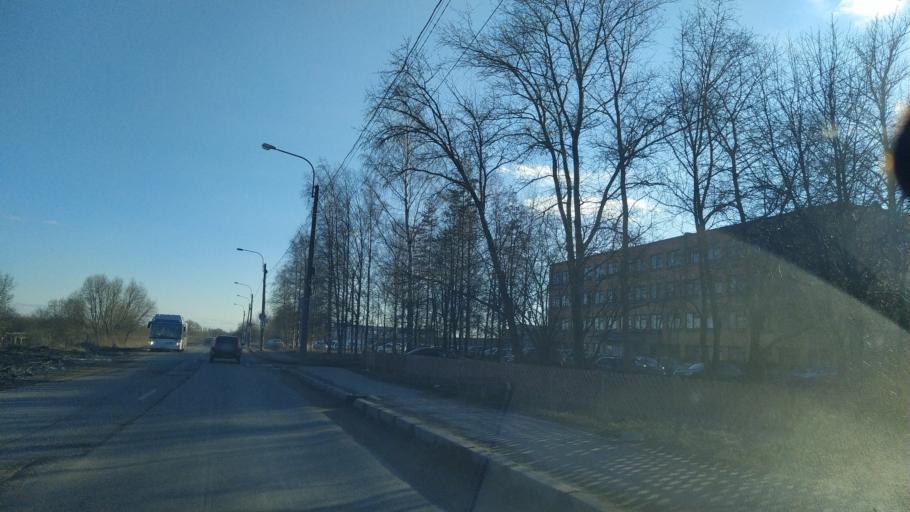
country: RU
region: St.-Petersburg
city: Pushkin
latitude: 59.6973
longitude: 30.3952
